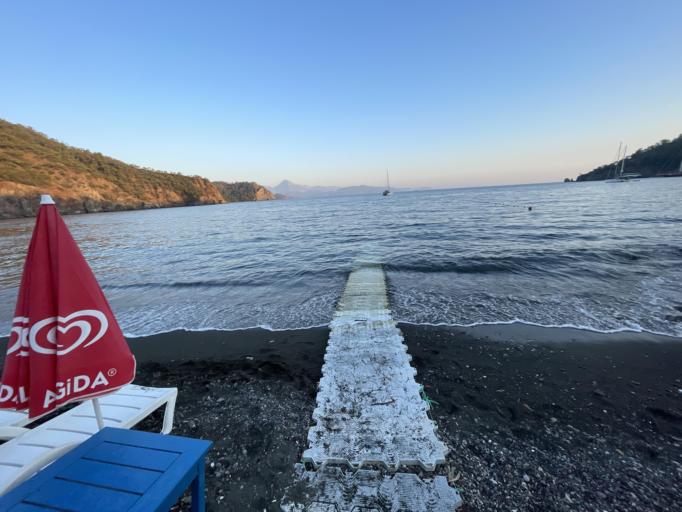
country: TR
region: Mugla
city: Goecek
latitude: 36.7310
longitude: 28.9675
